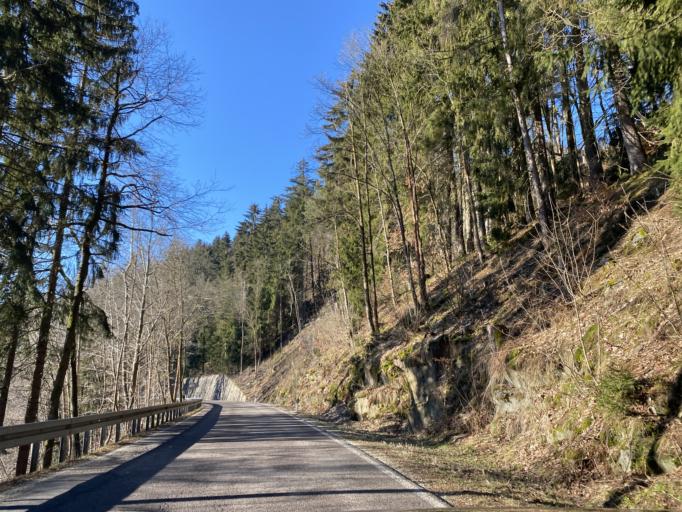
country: DE
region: Saxony
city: Thermalbad Wiesenbad
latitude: 50.6230
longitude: 13.0374
